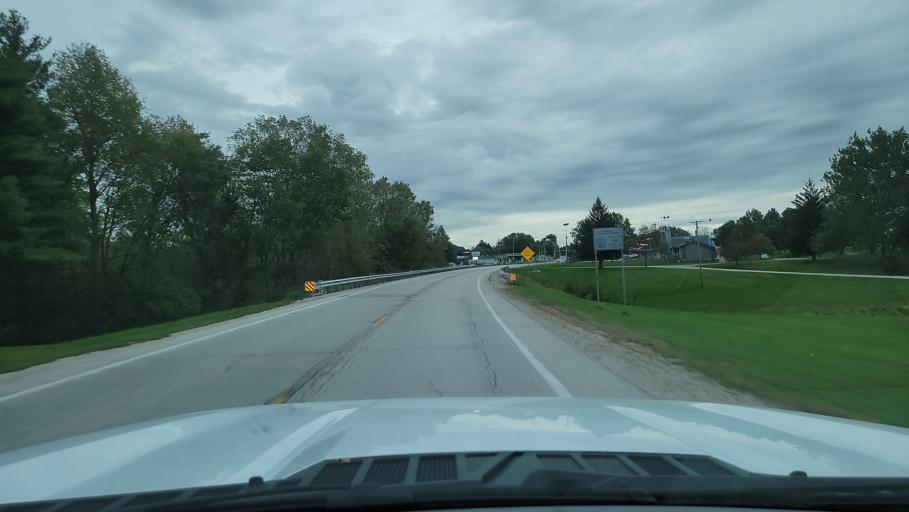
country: US
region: Illinois
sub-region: Schuyler County
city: Rushville
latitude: 40.1172
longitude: -90.5808
